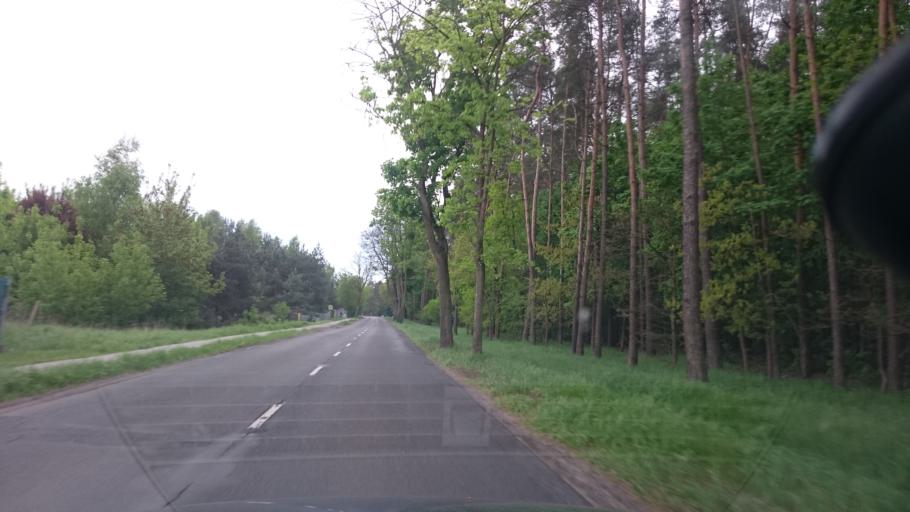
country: PL
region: Kujawsko-Pomorskie
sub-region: Grudziadz
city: Grudziadz
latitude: 53.4565
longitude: 18.7741
